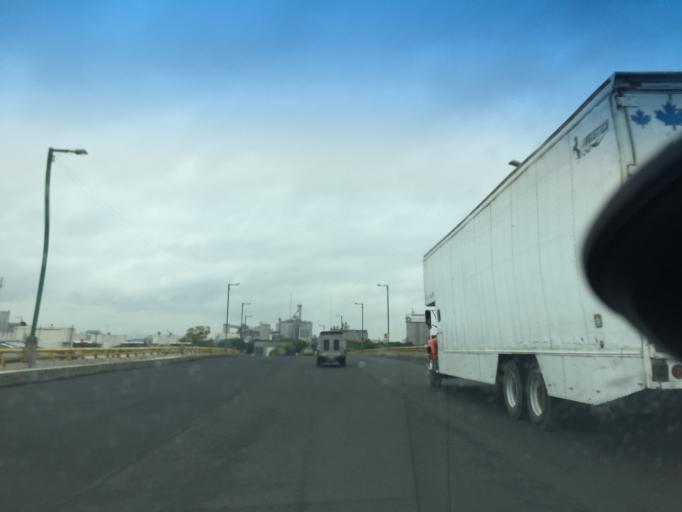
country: MX
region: Mexico City
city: Azcapotzalco
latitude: 19.4999
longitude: -99.1737
